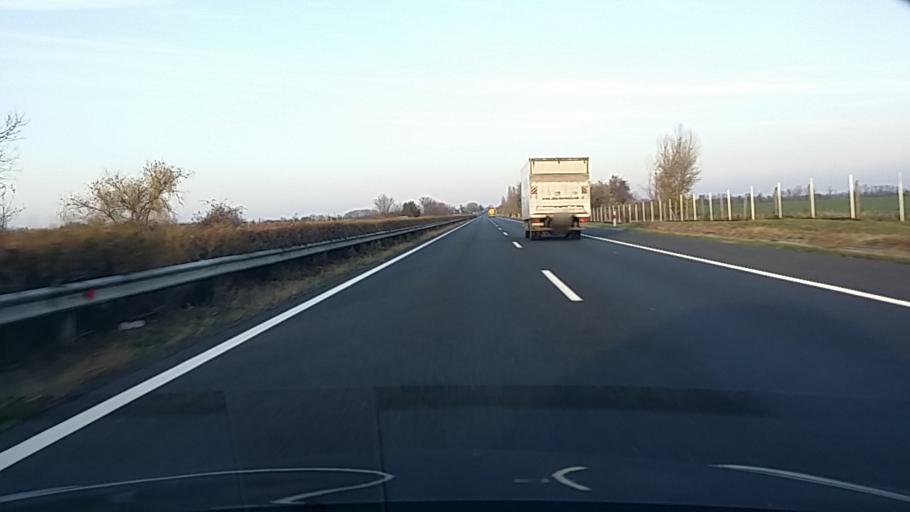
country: HU
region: Fejer
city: Polgardi
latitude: 47.0709
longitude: 18.3457
